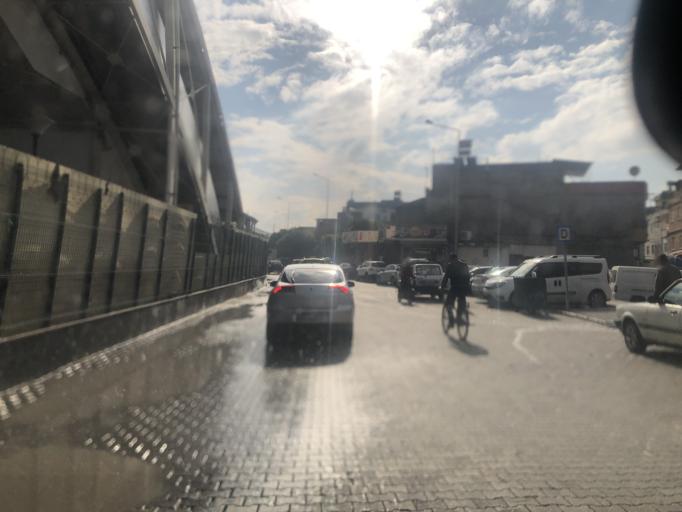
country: TR
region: Adana
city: Seyhan
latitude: 36.9846
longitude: 35.3192
